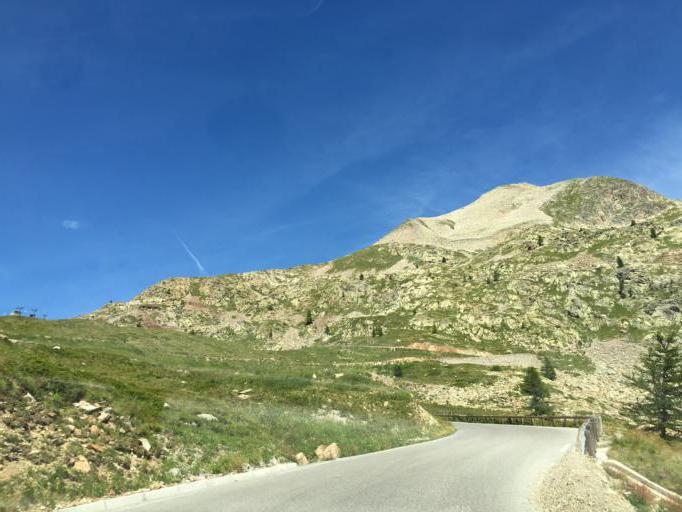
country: IT
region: Piedmont
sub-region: Provincia di Cuneo
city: Vinadio
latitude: 44.1982
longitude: 7.1550
